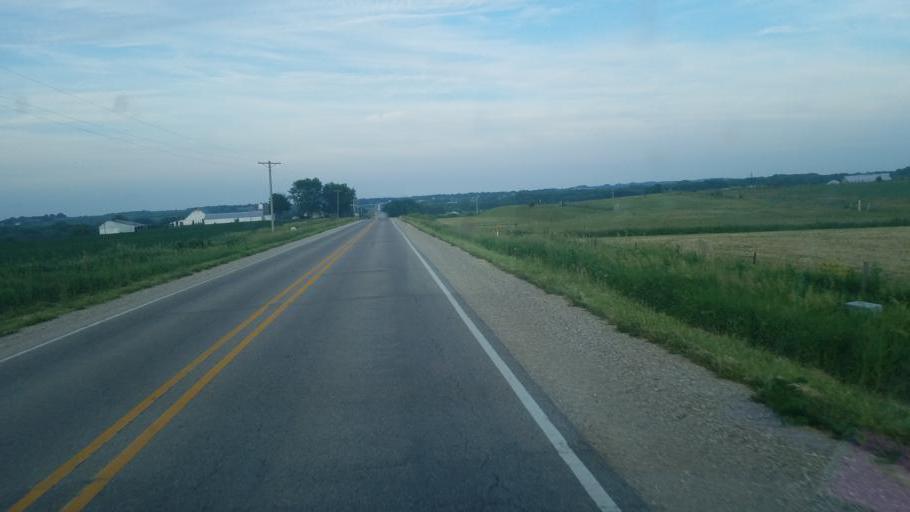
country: US
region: Iowa
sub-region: Benton County
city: Belle Plaine
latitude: 41.9060
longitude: -92.3214
